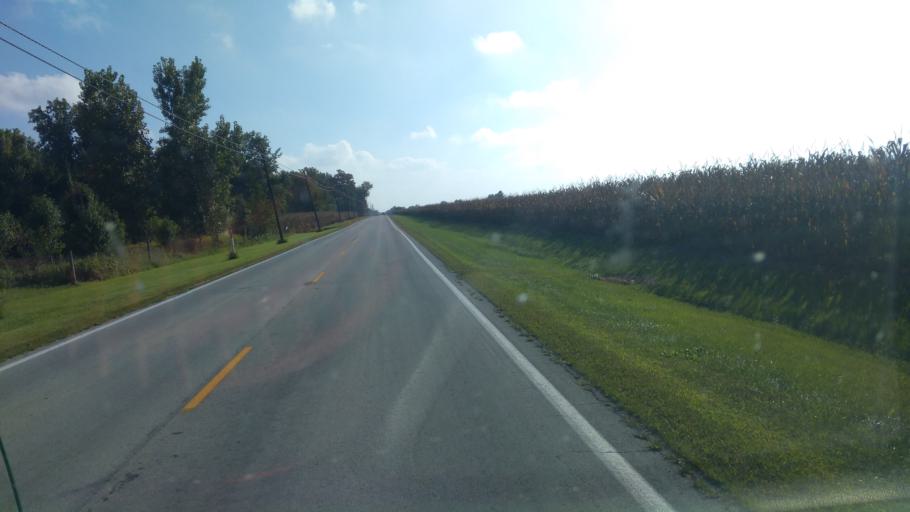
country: US
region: Ohio
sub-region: Hardin County
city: Forest
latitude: 40.7936
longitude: -83.5176
